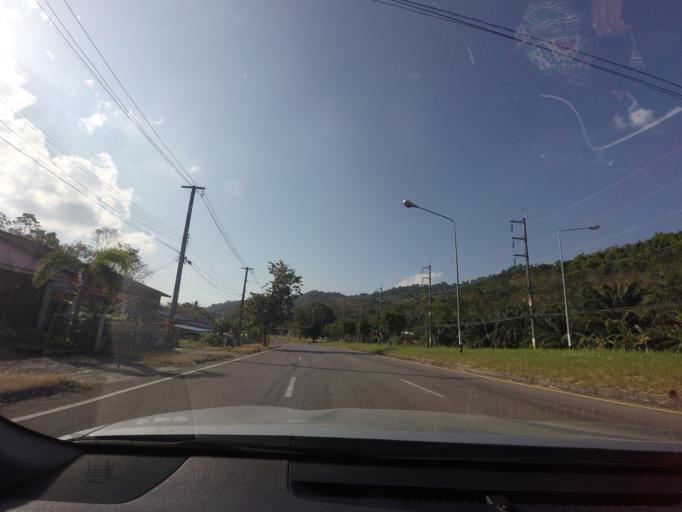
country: TH
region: Phangnga
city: Thai Mueang
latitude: 8.2713
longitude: 98.3368
